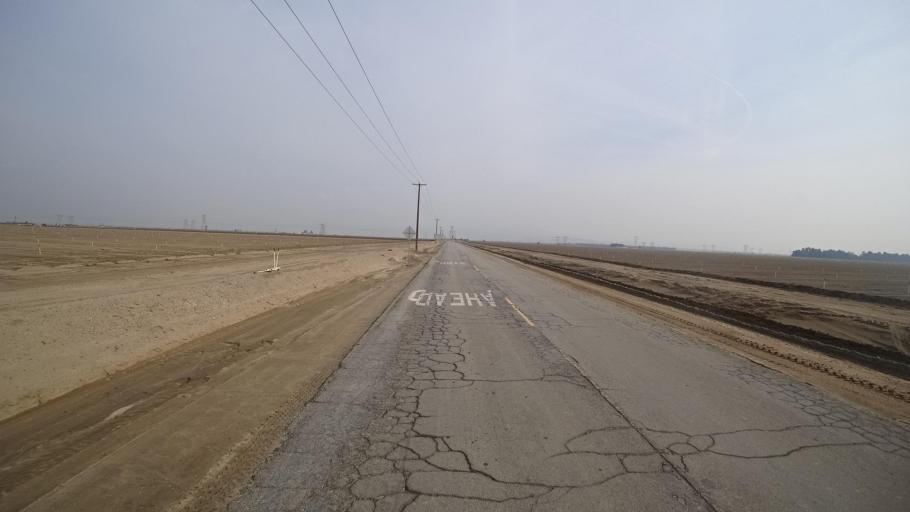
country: US
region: California
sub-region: Kern County
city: Weedpatch
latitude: 35.1511
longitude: -118.9126
